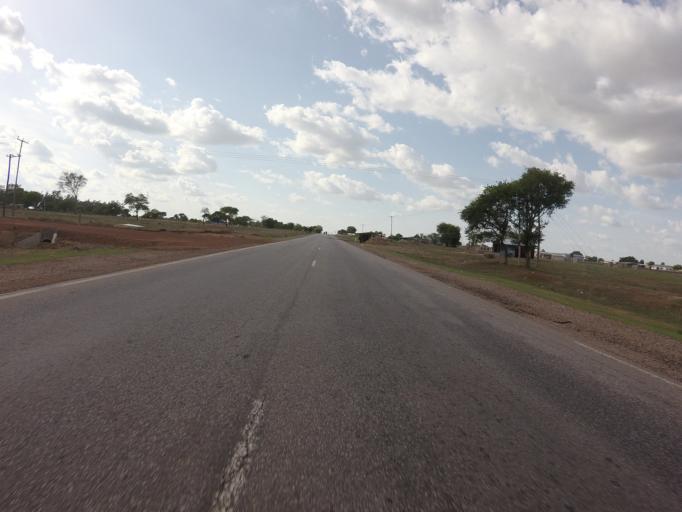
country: GH
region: Upper East
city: Bolgatanga
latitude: 10.6736
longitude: -0.8612
